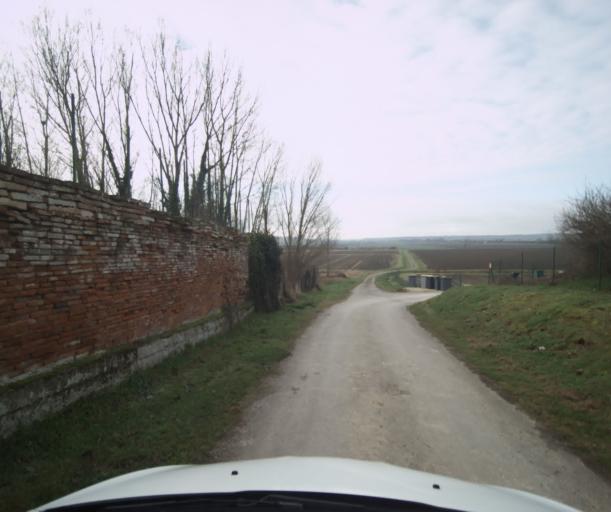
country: FR
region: Midi-Pyrenees
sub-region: Departement du Tarn-et-Garonne
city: Saint-Porquier
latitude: 44.0235
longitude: 1.1480
